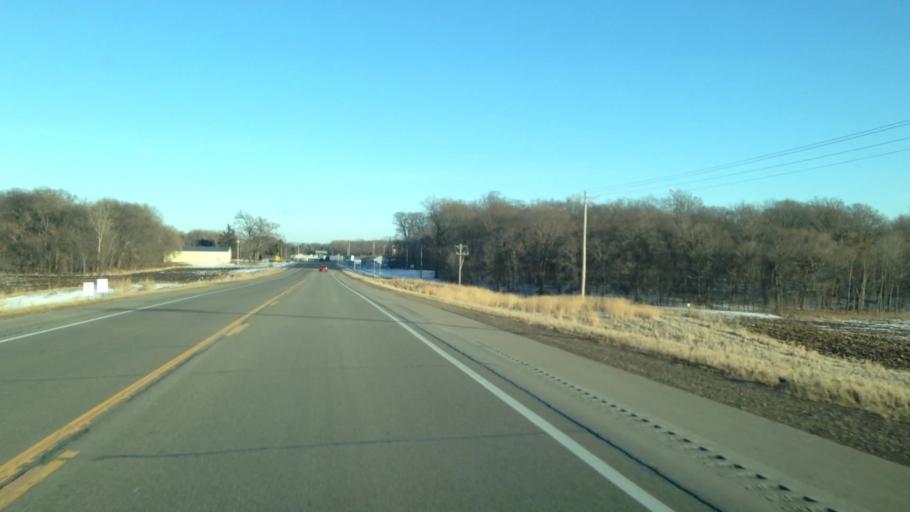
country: US
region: Minnesota
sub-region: Scott County
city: Elko New Market
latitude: 44.4718
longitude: -93.3029
